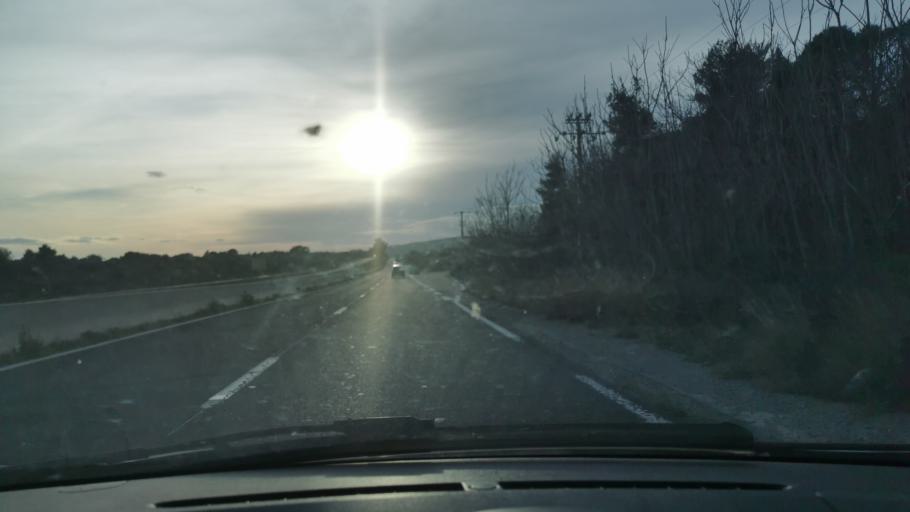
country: FR
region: Languedoc-Roussillon
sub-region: Departement de l'Herault
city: Mireval
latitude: 43.5255
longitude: 3.8183
